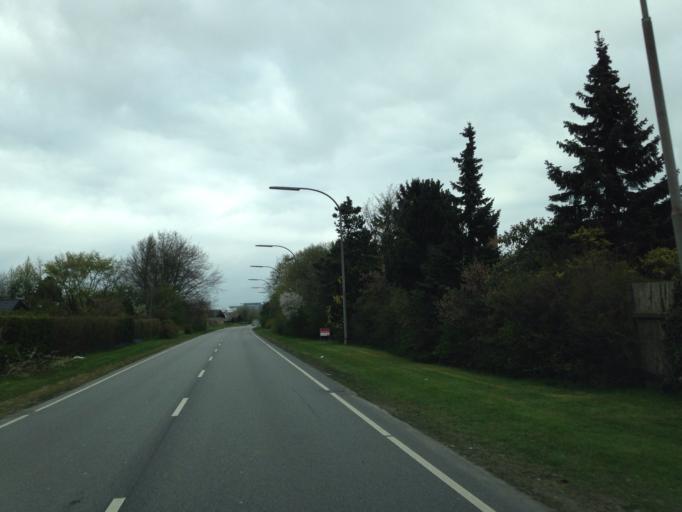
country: DK
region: Zealand
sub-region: Greve Kommune
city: Greve
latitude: 55.5777
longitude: 12.2825
